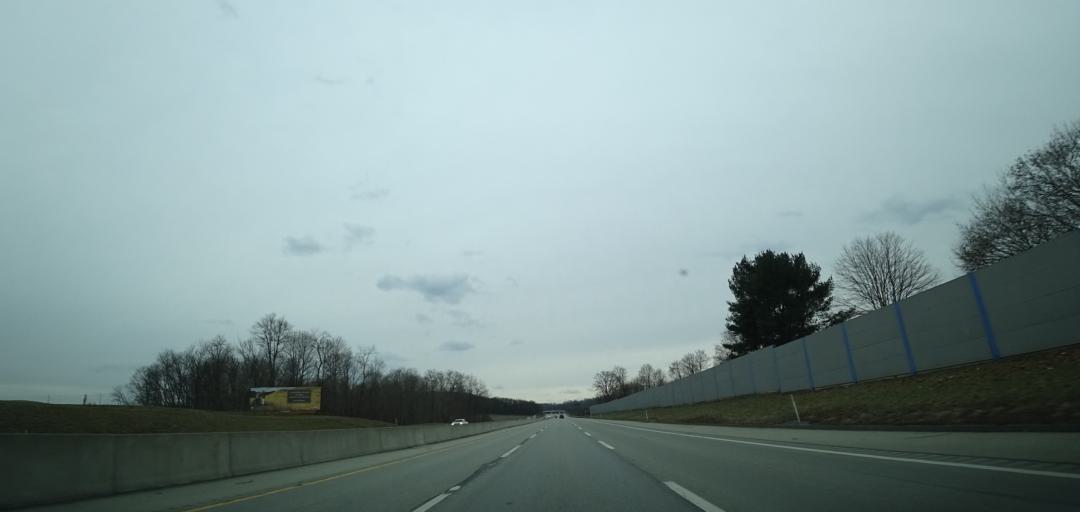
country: US
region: Pennsylvania
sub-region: Lawrence County
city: New Beaver
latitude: 40.8613
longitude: -80.3986
